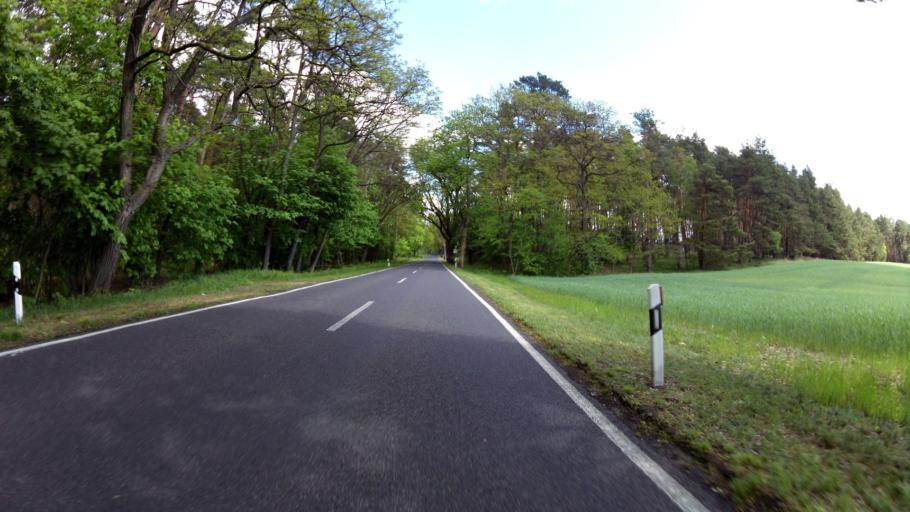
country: DE
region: Brandenburg
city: Wendisch Rietz
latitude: 52.1609
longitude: 14.0309
